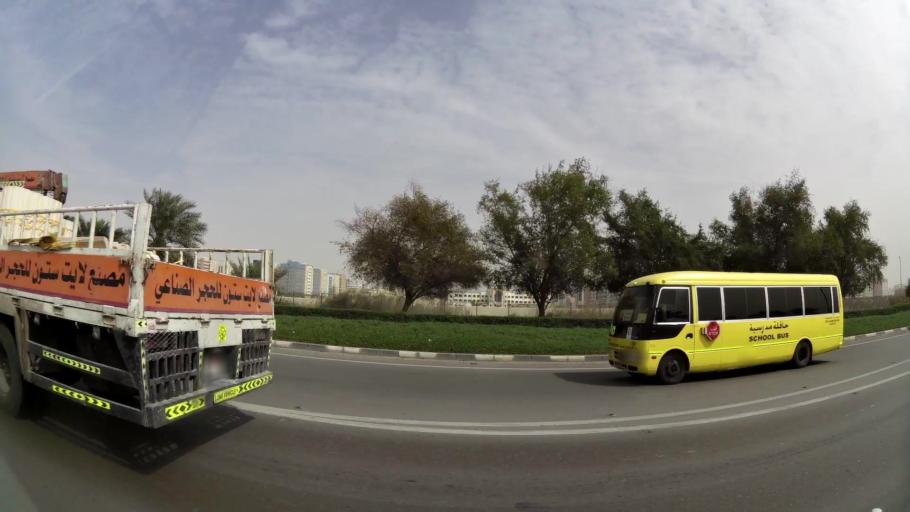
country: AE
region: Abu Dhabi
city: Abu Dhabi
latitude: 24.3386
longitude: 54.5267
